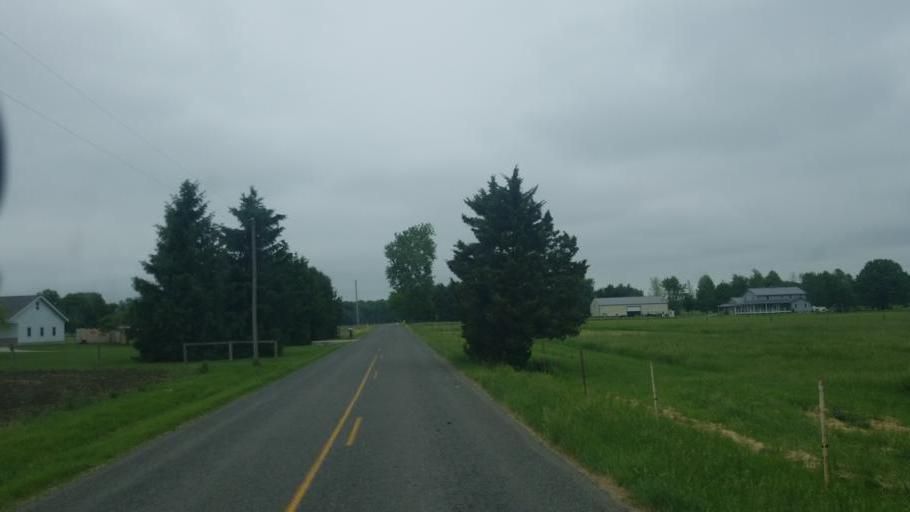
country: US
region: Indiana
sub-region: Elkhart County
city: Nappanee
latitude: 41.4672
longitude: -86.0497
